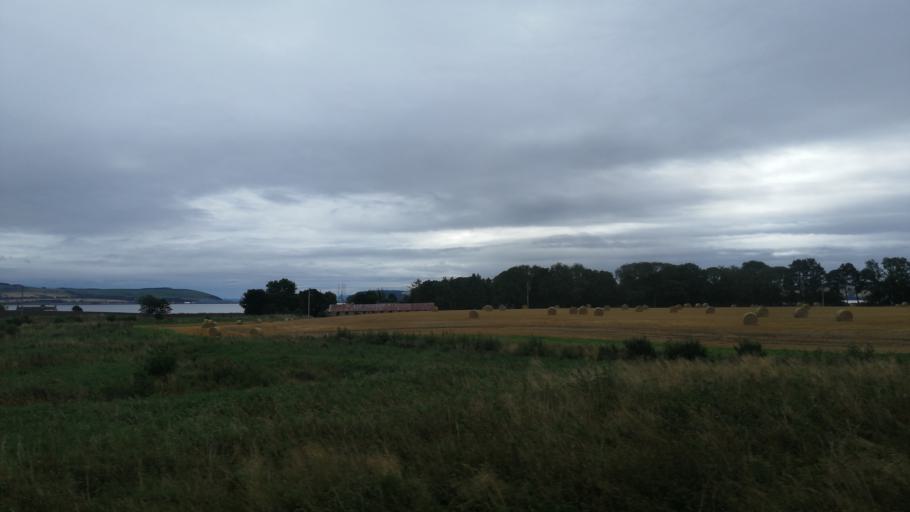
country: GB
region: Scotland
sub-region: Highland
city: Invergordon
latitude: 57.7213
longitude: -4.1153
